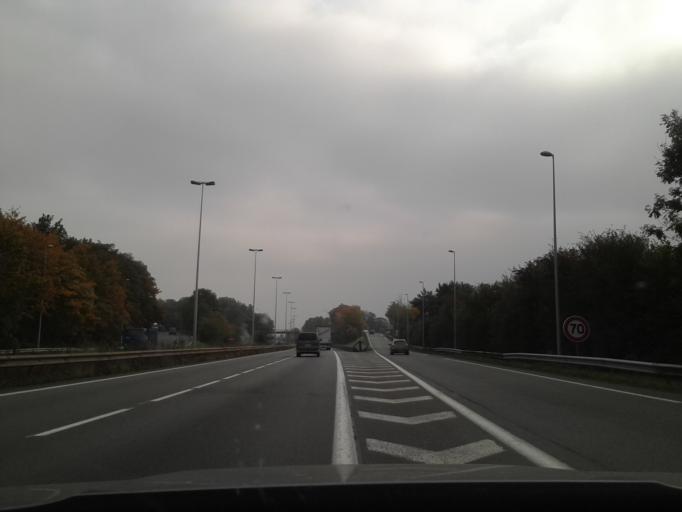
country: FR
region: Nord-Pas-de-Calais
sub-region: Departement du Nord
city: Baisieux
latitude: 50.6012
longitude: 3.2474
